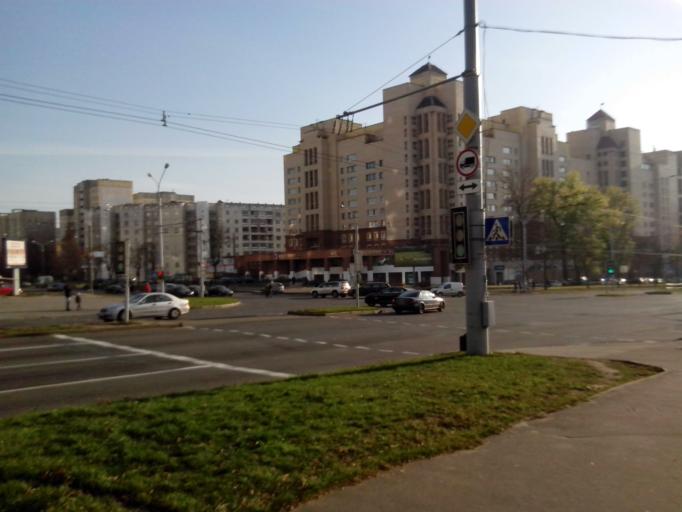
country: BY
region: Minsk
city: Minsk
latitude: 53.9362
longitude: 27.5816
